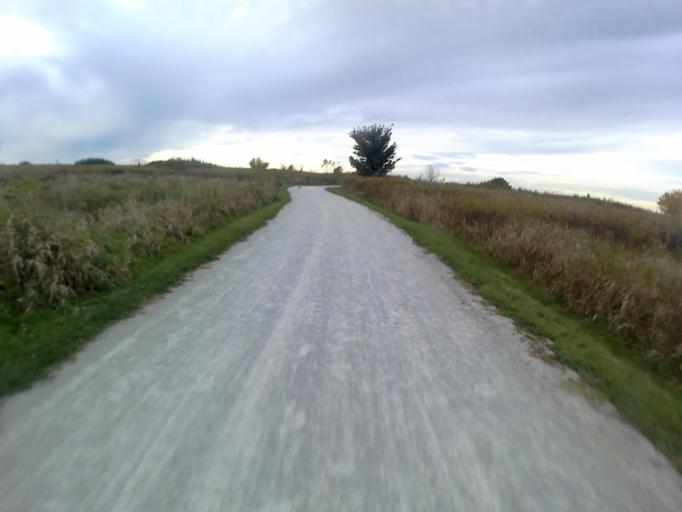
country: US
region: Illinois
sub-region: DuPage County
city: Lisle
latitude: 41.8223
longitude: -88.1032
